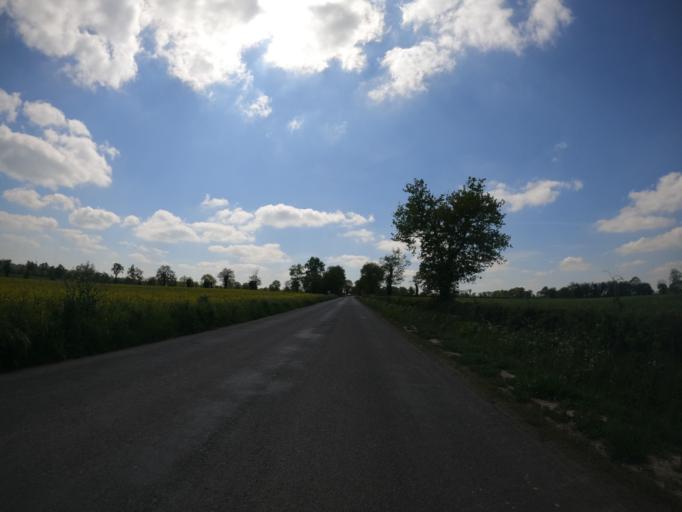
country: FR
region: Poitou-Charentes
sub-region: Departement des Deux-Sevres
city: Chiche
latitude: 46.7329
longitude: -0.3697
